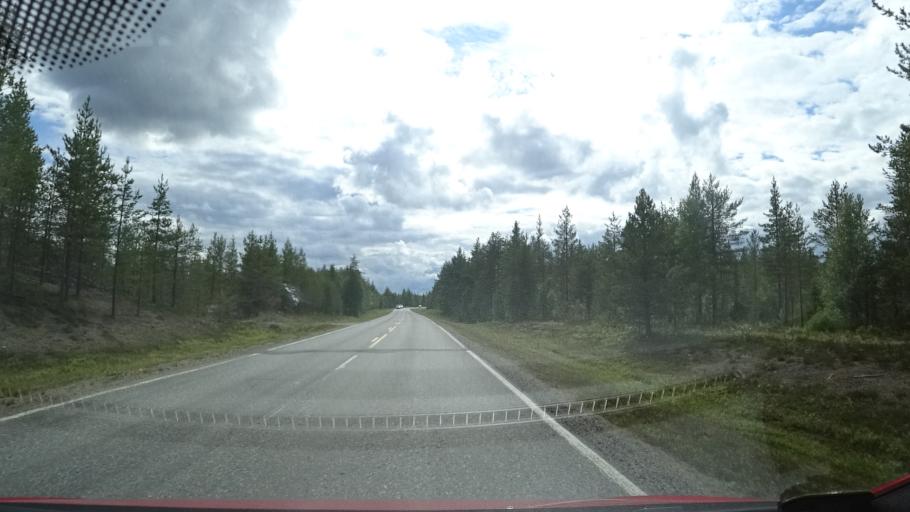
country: FI
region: Lapland
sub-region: Tunturi-Lappi
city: Kittilae
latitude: 67.5059
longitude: 24.8990
